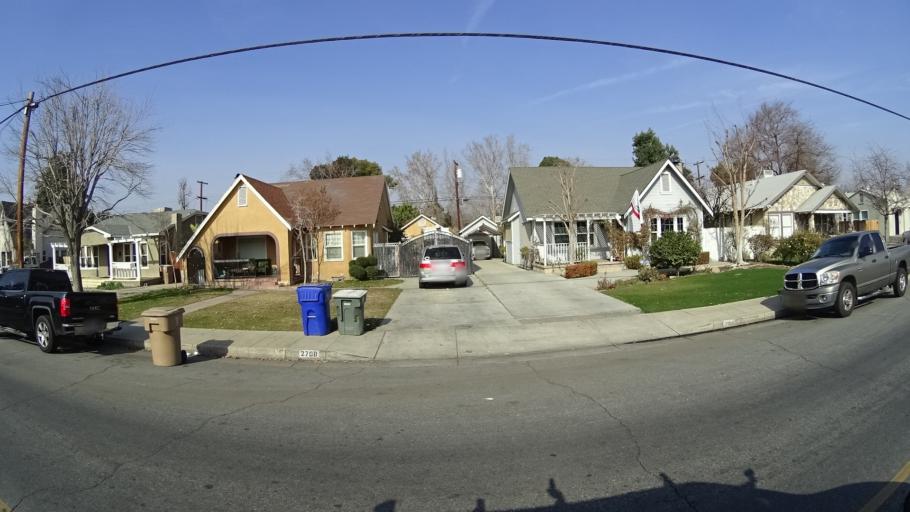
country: US
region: California
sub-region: Kern County
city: Bakersfield
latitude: 35.3649
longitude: -119.0330
